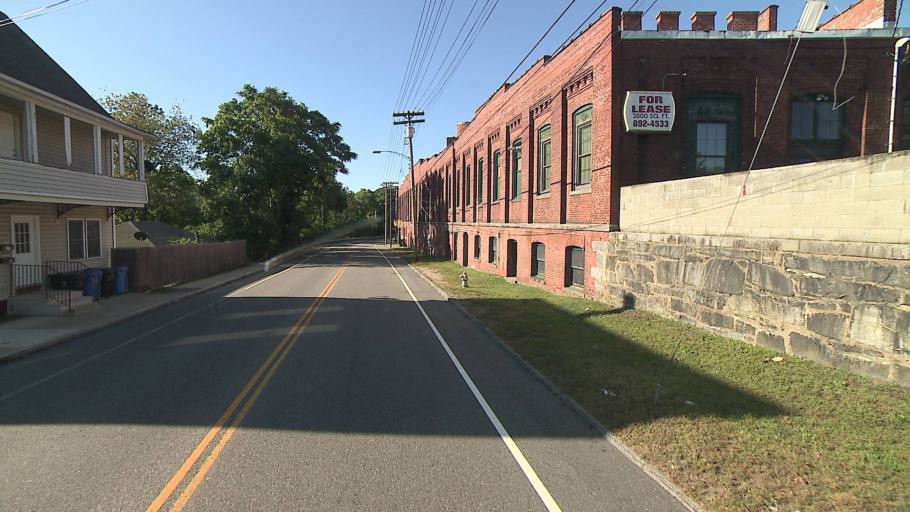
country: US
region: Connecticut
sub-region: New London County
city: Norwich
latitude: 41.5390
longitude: -72.0528
